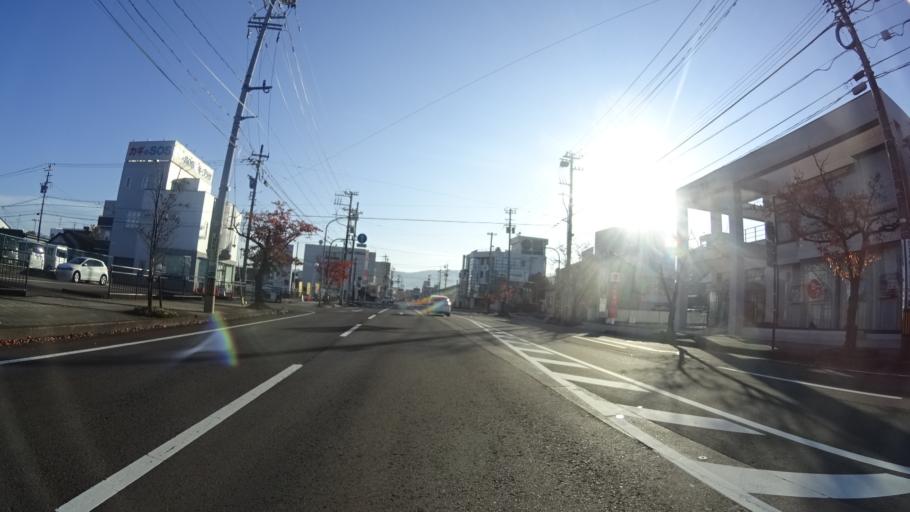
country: JP
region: Fukui
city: Fukui-shi
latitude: 36.0635
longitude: 136.2407
